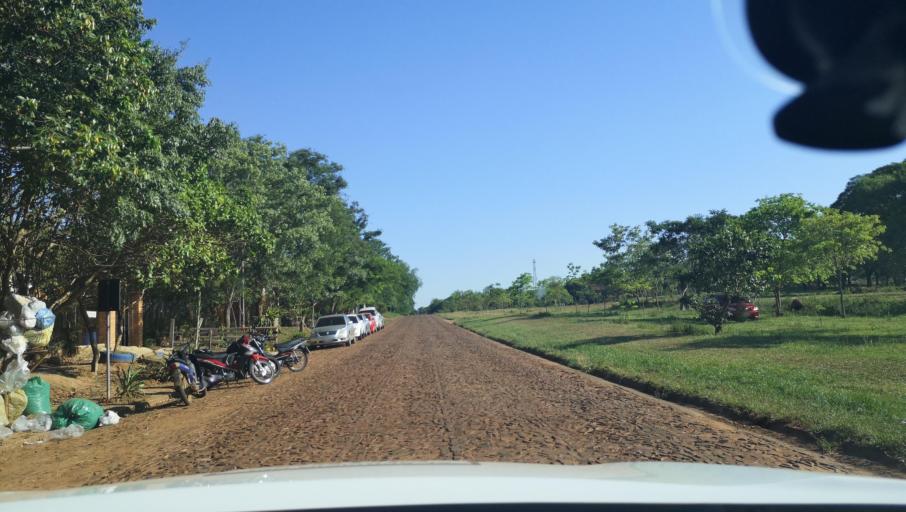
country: PY
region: Itapua
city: Carmen del Parana
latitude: -27.1686
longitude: -56.2400
